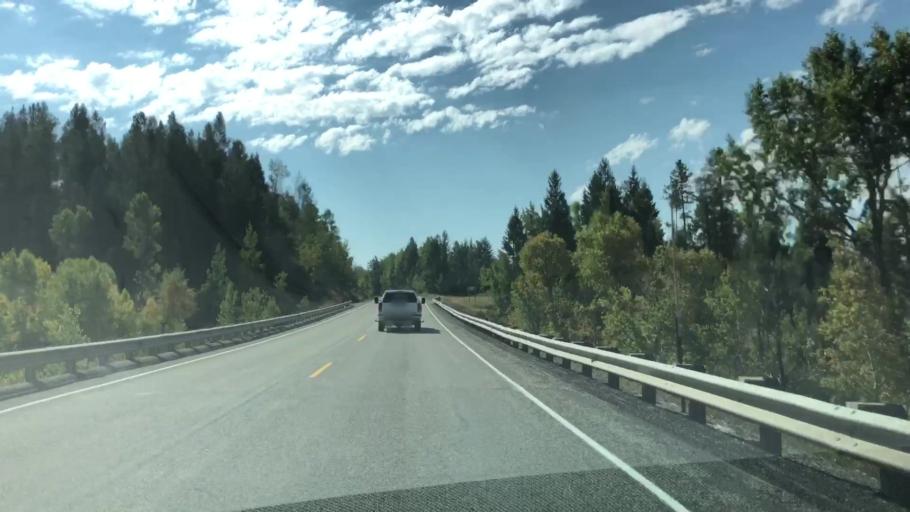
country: US
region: Idaho
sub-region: Teton County
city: Victor
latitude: 43.2832
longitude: -111.1195
